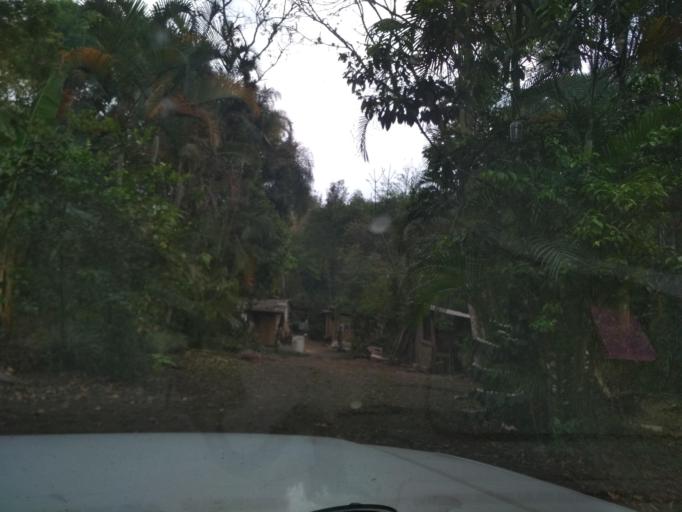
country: MX
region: Veracruz
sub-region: Cordoba
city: San Jose de Tapia
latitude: 18.8351
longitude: -96.9807
